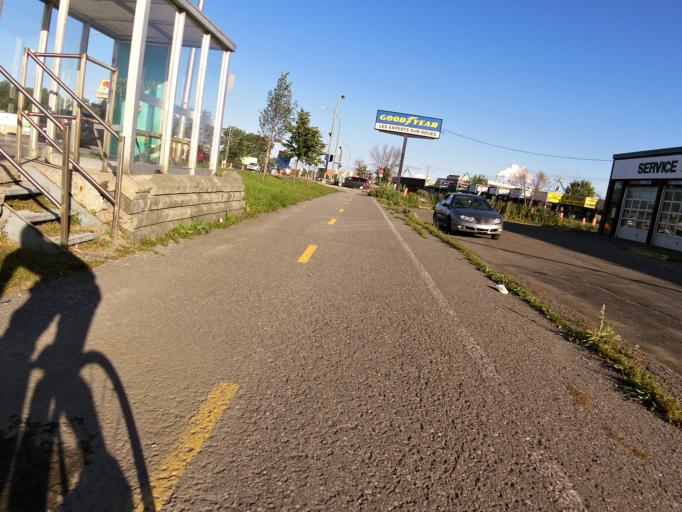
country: CA
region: Quebec
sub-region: Outaouais
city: Gatineau
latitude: 45.4838
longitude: -75.6630
